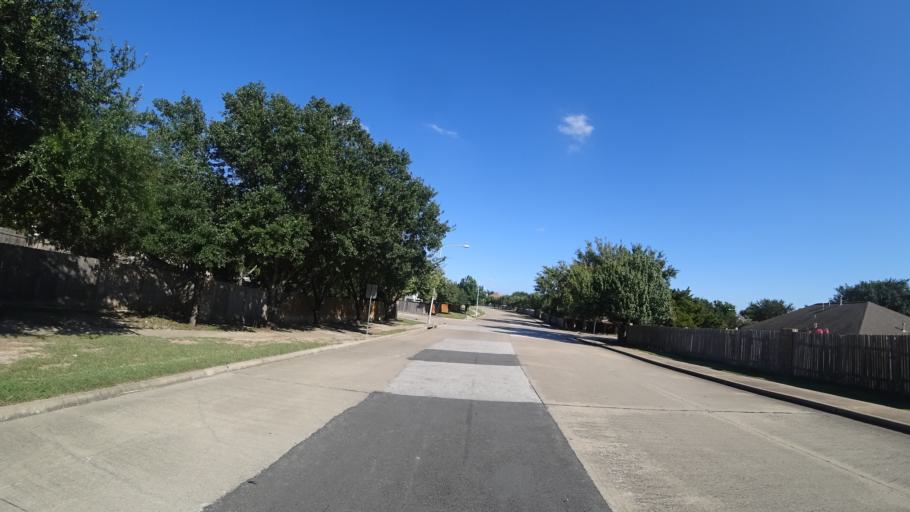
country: US
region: Texas
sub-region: Travis County
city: Manor
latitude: 30.3531
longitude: -97.6134
